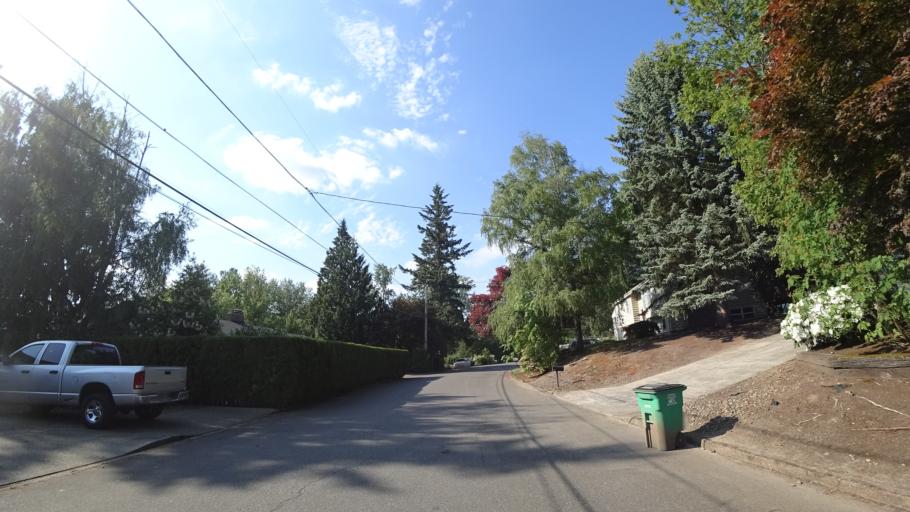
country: US
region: Oregon
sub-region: Washington County
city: Garden Home-Whitford
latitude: 45.4615
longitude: -122.7357
